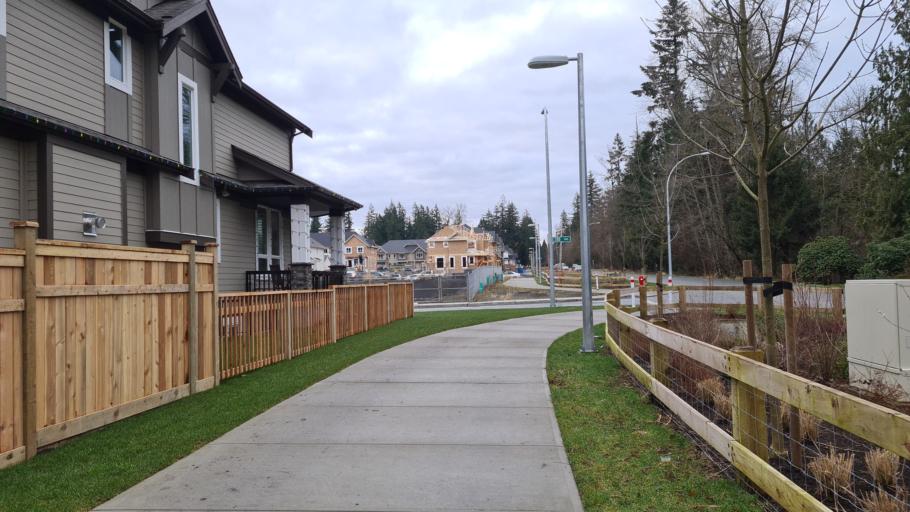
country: CA
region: British Columbia
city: Walnut Grove
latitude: 49.1463
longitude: -122.6568
